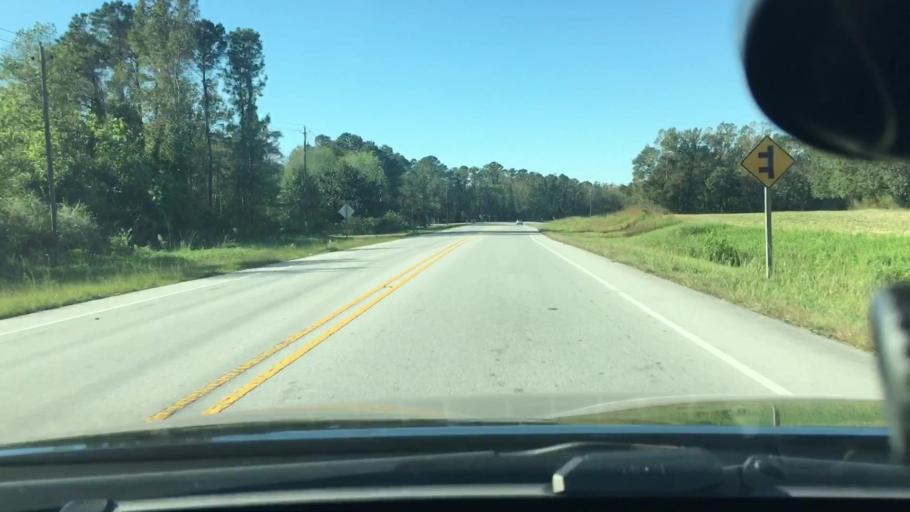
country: US
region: North Carolina
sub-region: Craven County
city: Trent Woods
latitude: 35.1721
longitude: -77.1286
